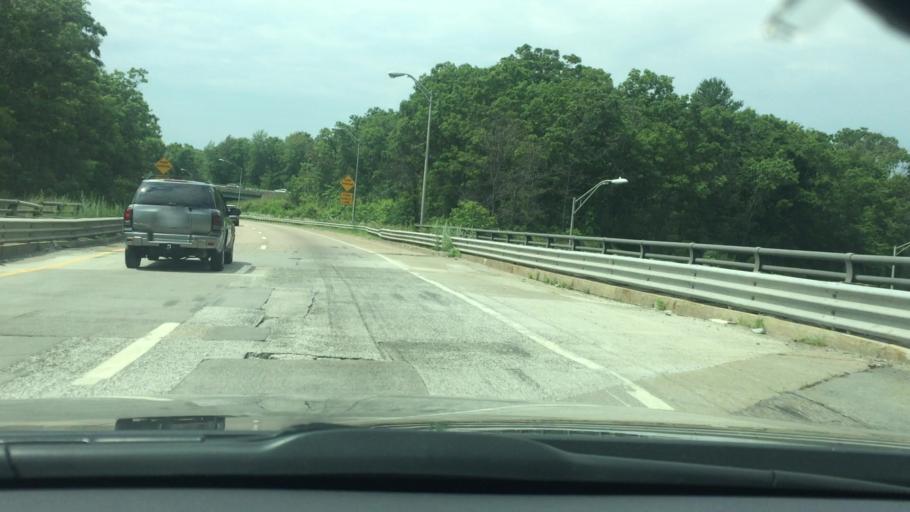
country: US
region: Massachusetts
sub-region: Norfolk County
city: Milton
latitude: 42.2011
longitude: -71.0790
